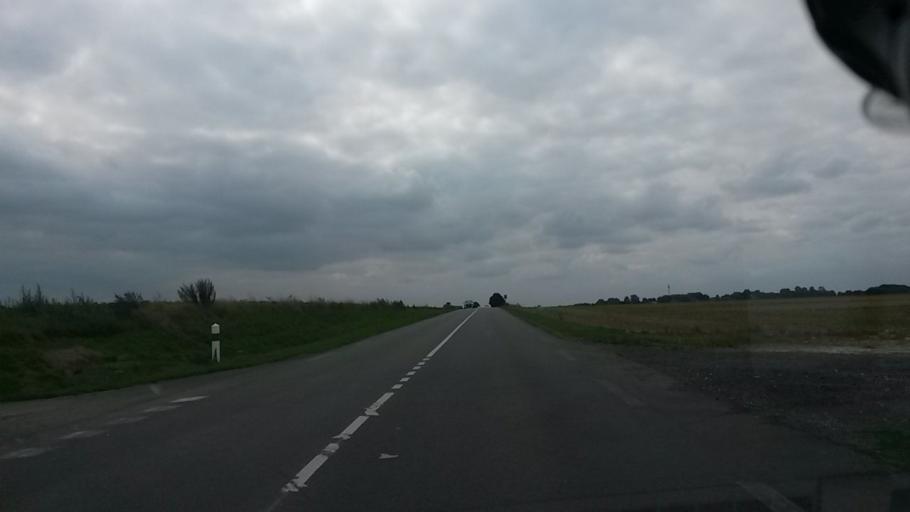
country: FR
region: Picardie
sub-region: Departement de la Somme
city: Corbie
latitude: 49.9676
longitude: 2.5311
